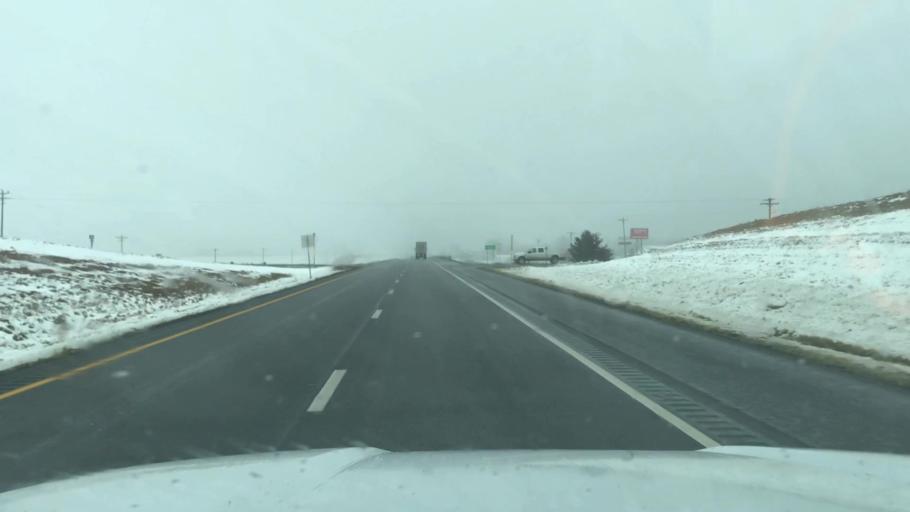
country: US
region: Missouri
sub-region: Clinton County
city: Gower
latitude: 39.7620
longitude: -94.5091
